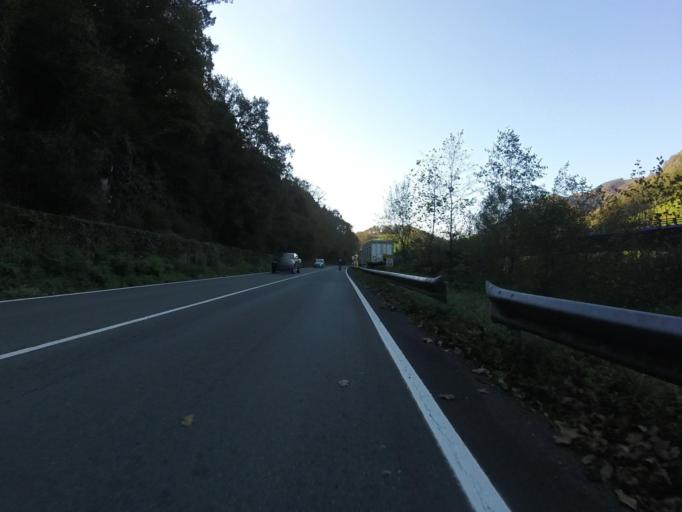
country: ES
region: Navarre
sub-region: Provincia de Navarra
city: Lesaka
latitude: 43.2451
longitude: -1.6690
